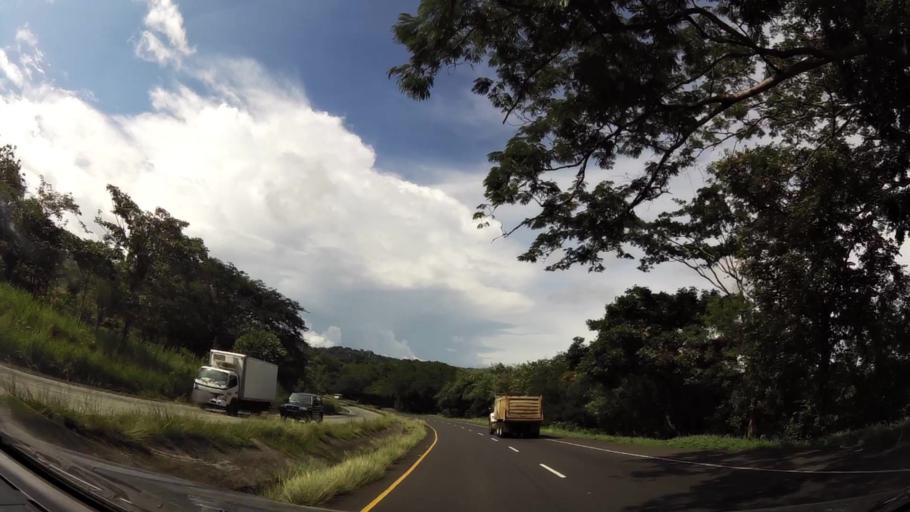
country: PA
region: Panama
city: Capira
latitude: 8.6991
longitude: -79.8669
